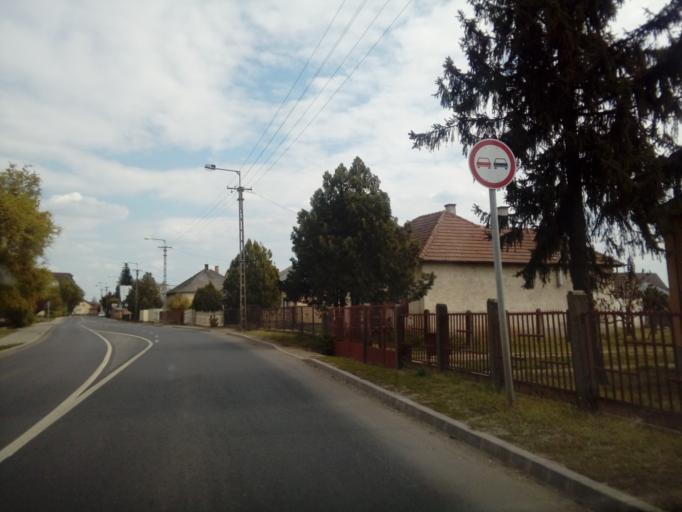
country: HU
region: Szabolcs-Szatmar-Bereg
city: Nagykallo
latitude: 47.8774
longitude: 21.8355
